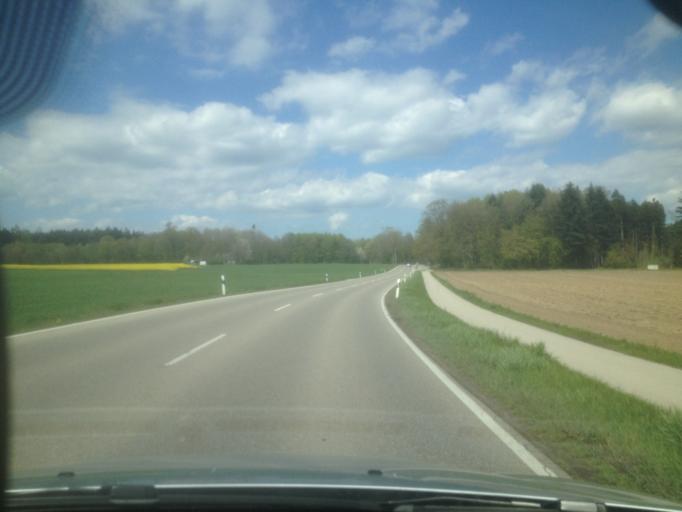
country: DE
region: Bavaria
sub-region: Swabia
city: Aystetten
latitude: 48.3817
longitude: 10.7488
